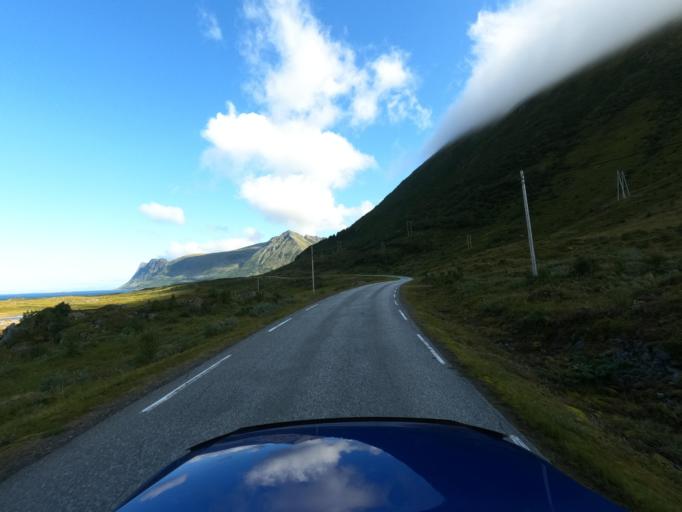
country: NO
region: Nordland
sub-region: Vagan
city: Kabelvag
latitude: 68.2677
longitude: 14.2853
